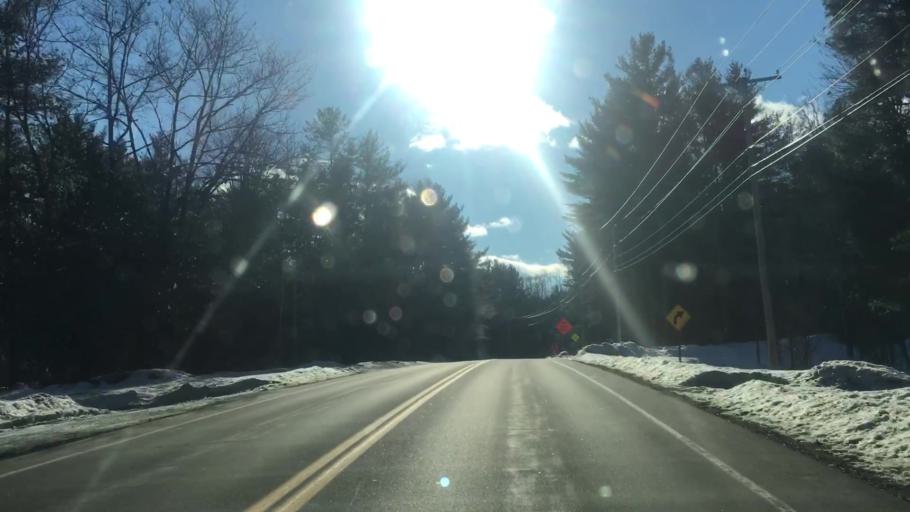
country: US
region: Maine
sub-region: Somerset County
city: Madison
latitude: 44.9407
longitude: -69.8655
